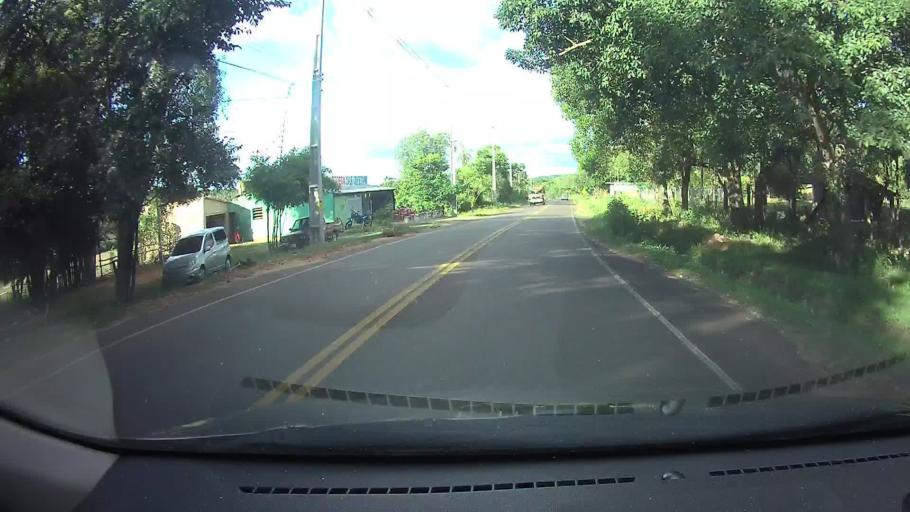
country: PY
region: Cordillera
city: Altos
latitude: -25.2466
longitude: -57.2346
